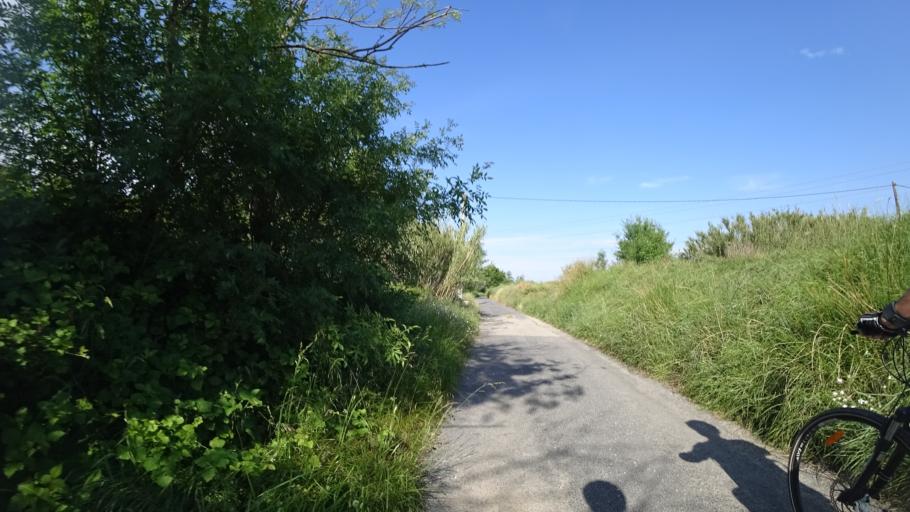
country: FR
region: Languedoc-Roussillon
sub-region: Departement de l'Herault
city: Olonzac
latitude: 43.2616
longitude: 2.7237
